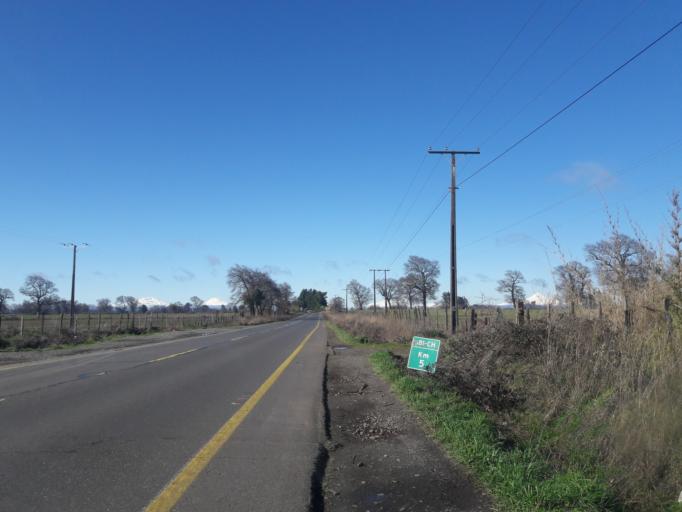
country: CL
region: Araucania
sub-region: Provincia de Malleco
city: Victoria
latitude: -38.2500
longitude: -72.3020
